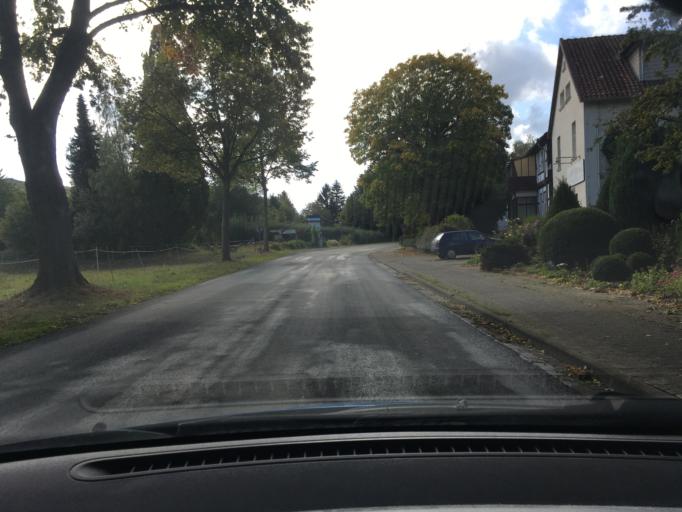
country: DE
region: Lower Saxony
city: Springe
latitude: 52.2027
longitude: 9.5379
